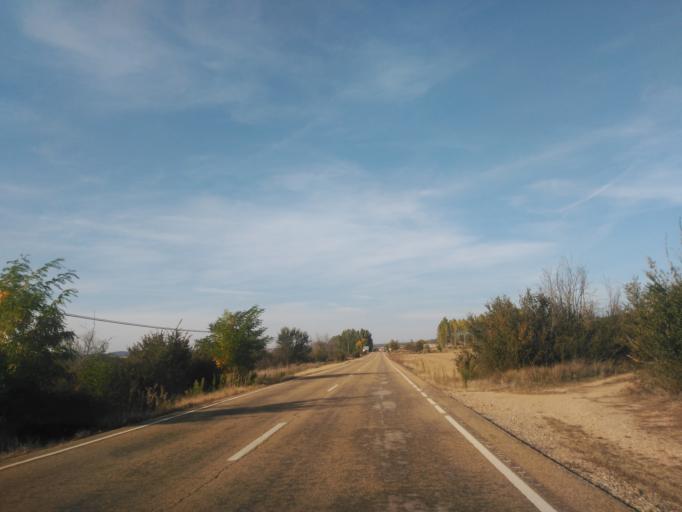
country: ES
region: Castille and Leon
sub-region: Provincia de Soria
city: Valdemaluque
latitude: 41.6635
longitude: -3.0495
